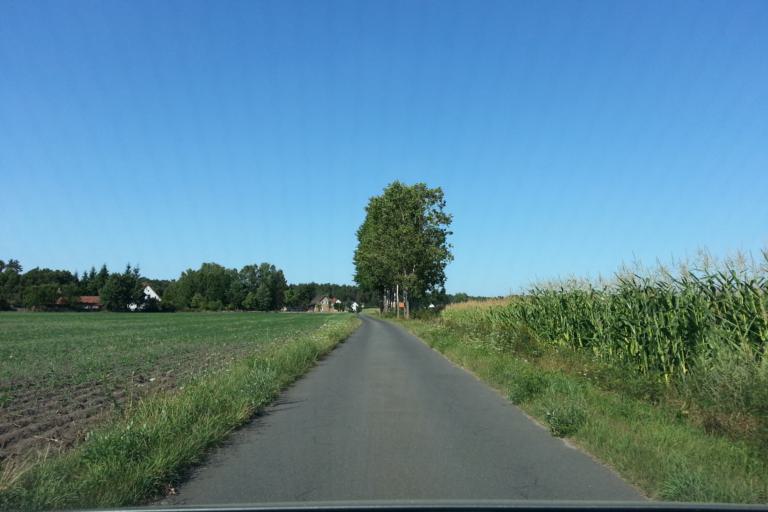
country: DE
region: Mecklenburg-Vorpommern
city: Eggesin
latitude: 53.6804
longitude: 14.0369
